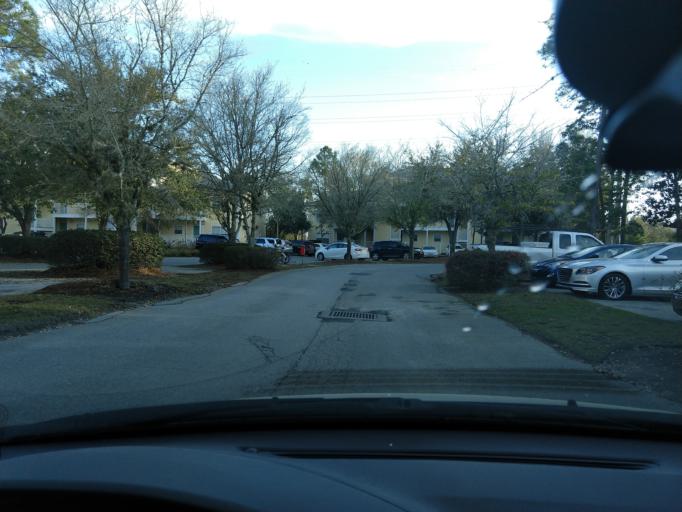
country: US
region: Florida
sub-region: Walton County
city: Miramar Beach
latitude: 30.3810
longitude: -86.3096
